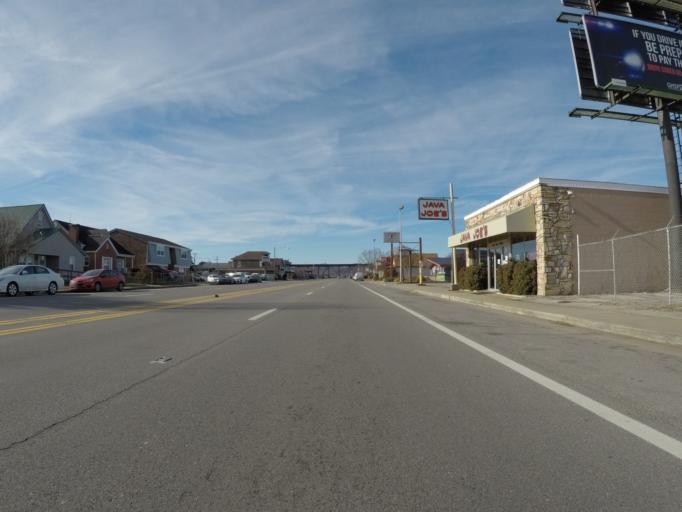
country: US
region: West Virginia
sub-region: Wayne County
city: Kenova
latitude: 38.3994
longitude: -82.5718
